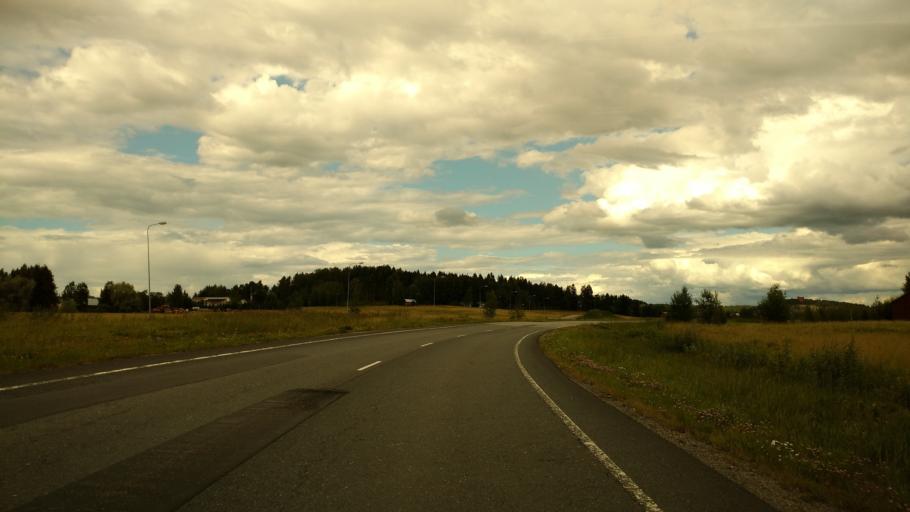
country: FI
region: Varsinais-Suomi
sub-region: Salo
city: Halikko
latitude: 60.3881
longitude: 23.0500
